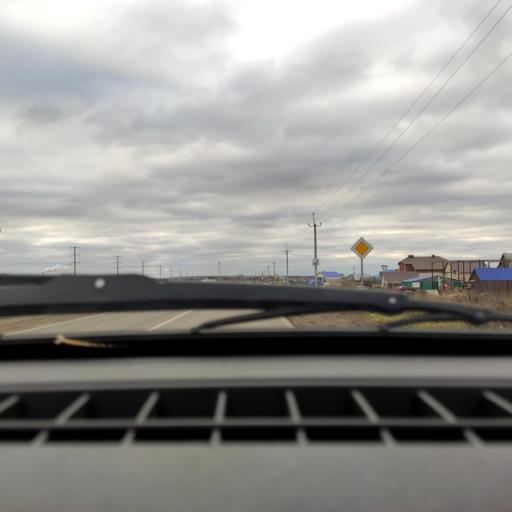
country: RU
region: Bashkortostan
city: Iglino
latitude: 54.7909
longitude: 56.2521
